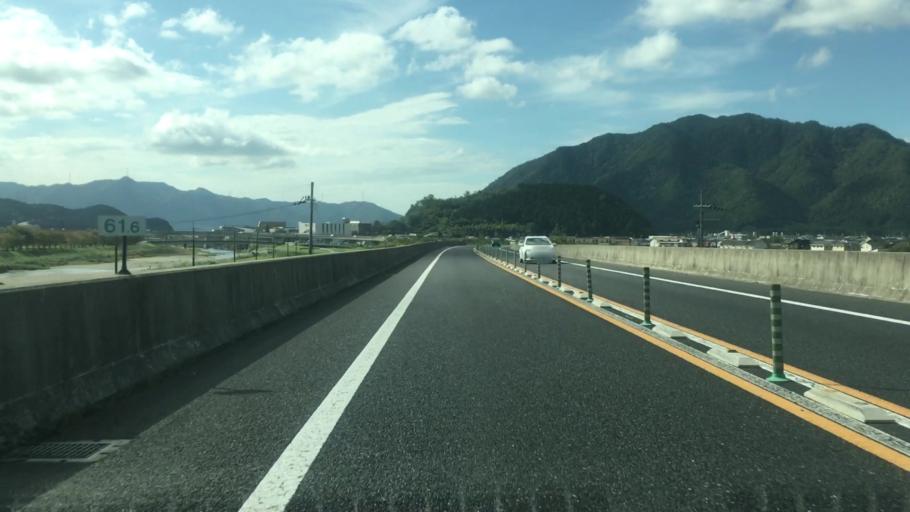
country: JP
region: Kyoto
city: Fukuchiyama
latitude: 35.1855
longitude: 135.0390
